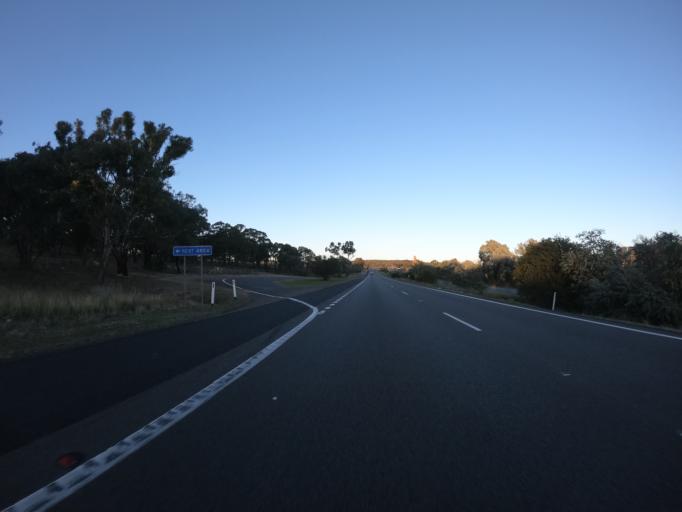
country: AU
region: New South Wales
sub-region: Goulburn Mulwaree
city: Goulburn
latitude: -34.7832
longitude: 149.6622
